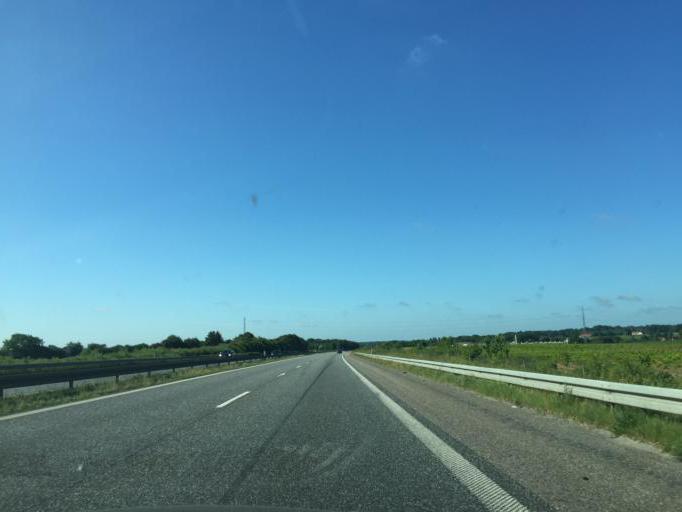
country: DK
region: South Denmark
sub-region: Haderslev Kommune
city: Haderslev
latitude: 55.2817
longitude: 9.4284
